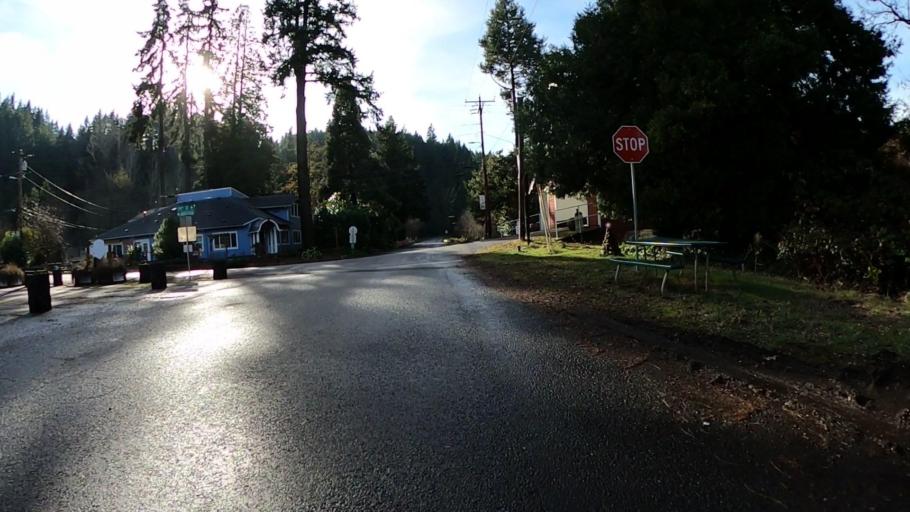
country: US
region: Oregon
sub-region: Lane County
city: Oakridge
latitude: 43.7586
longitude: -122.4951
